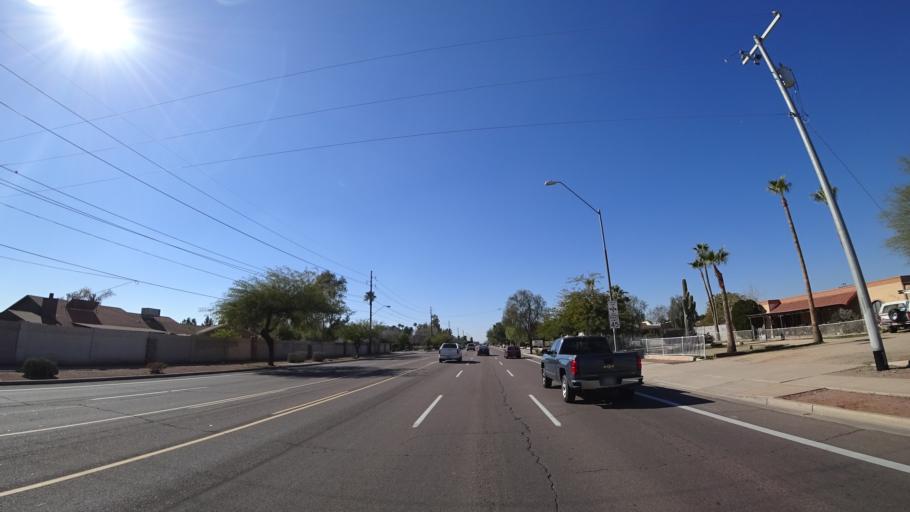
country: US
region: Arizona
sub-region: Maricopa County
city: Peoria
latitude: 33.6546
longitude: -112.1444
